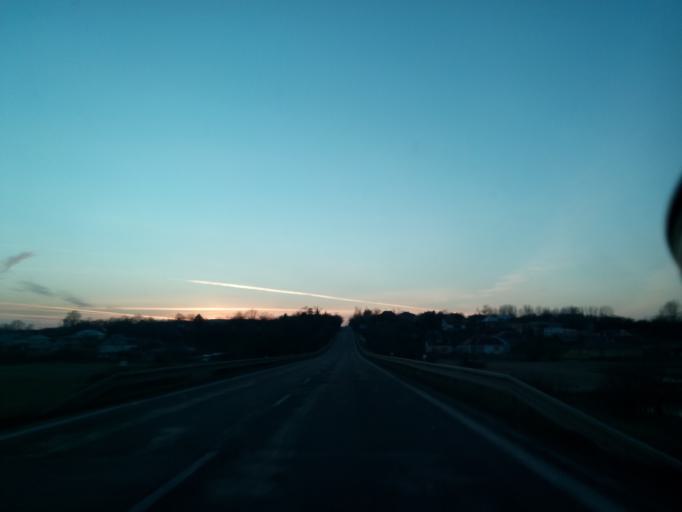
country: SK
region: Kosicky
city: Vinne
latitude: 48.7663
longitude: 22.0515
